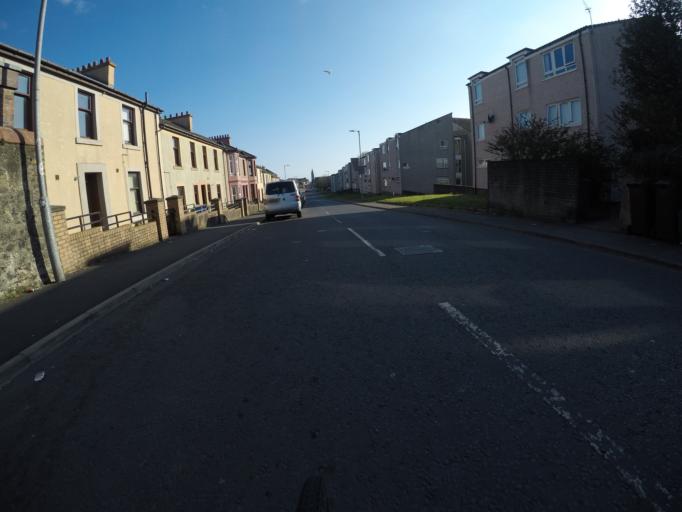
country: GB
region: Scotland
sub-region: North Ayrshire
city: Saltcoats
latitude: 55.6369
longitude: -4.7832
